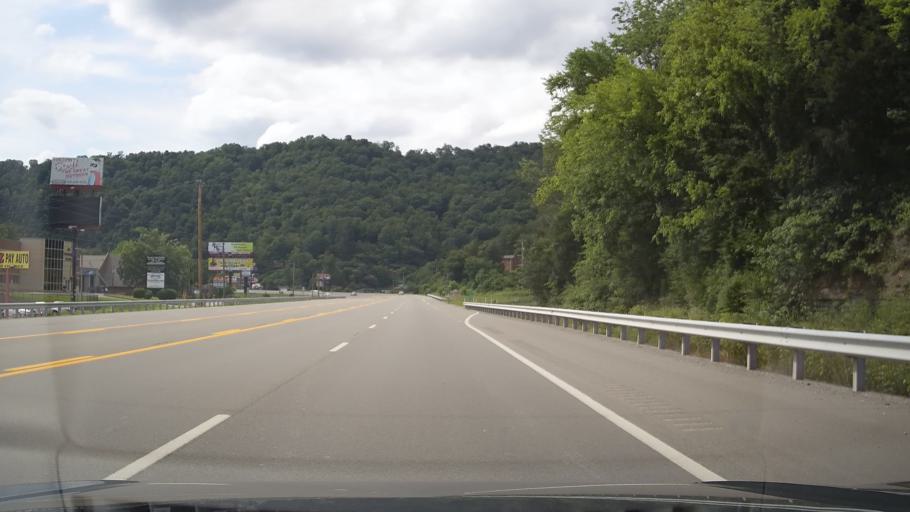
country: US
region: Kentucky
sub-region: Pike County
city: Coal Run Village
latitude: 37.5385
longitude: -82.5810
